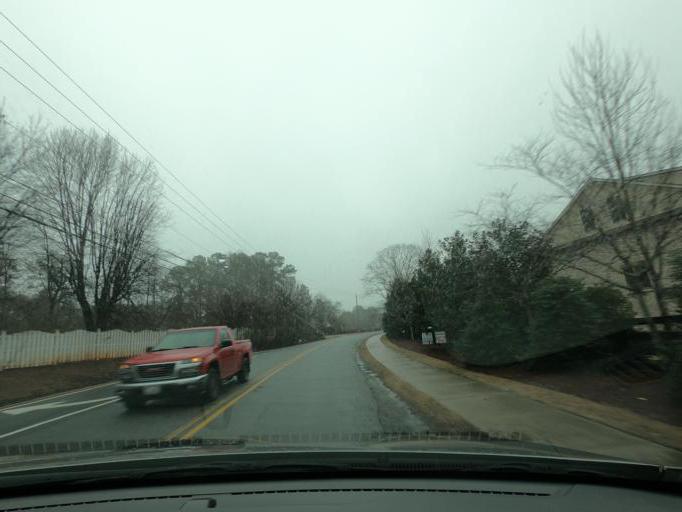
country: US
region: Georgia
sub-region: Fulton County
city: Alpharetta
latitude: 34.0959
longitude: -84.3299
